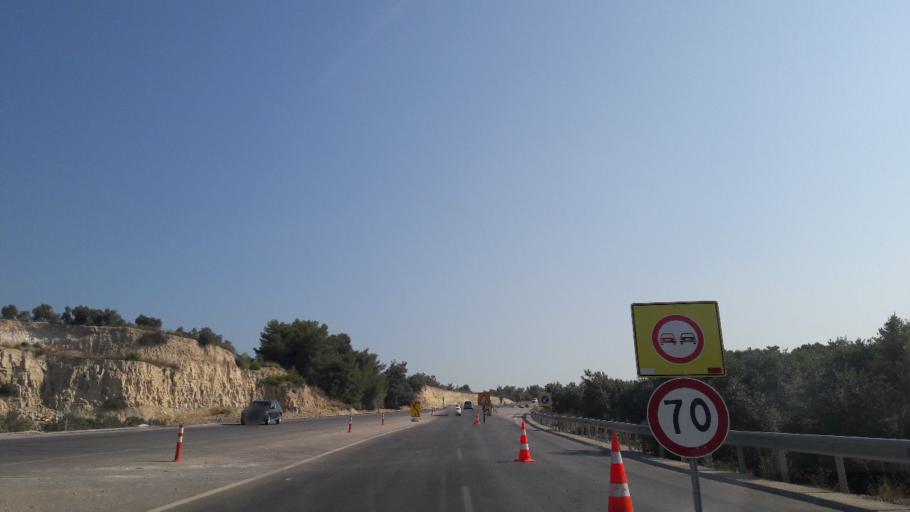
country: TR
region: Adana
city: Yuregir
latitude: 37.0796
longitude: 35.4738
